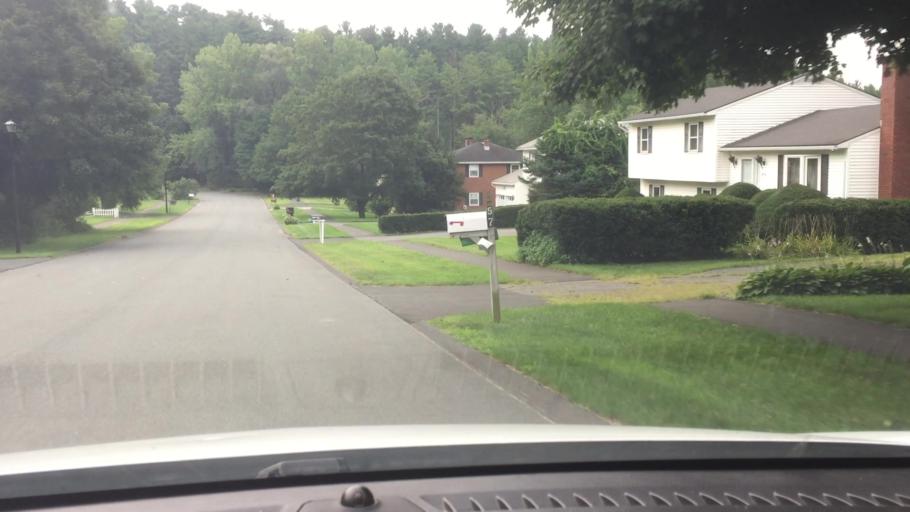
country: US
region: Massachusetts
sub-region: Berkshire County
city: Pittsfield
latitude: 42.4511
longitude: -73.2814
